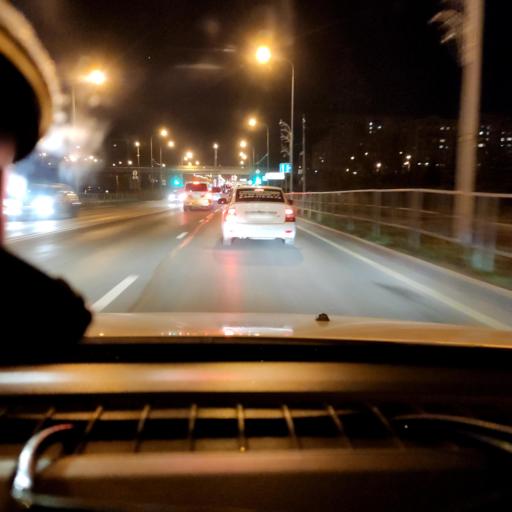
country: RU
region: Samara
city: Samara
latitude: 53.2707
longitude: 50.2232
